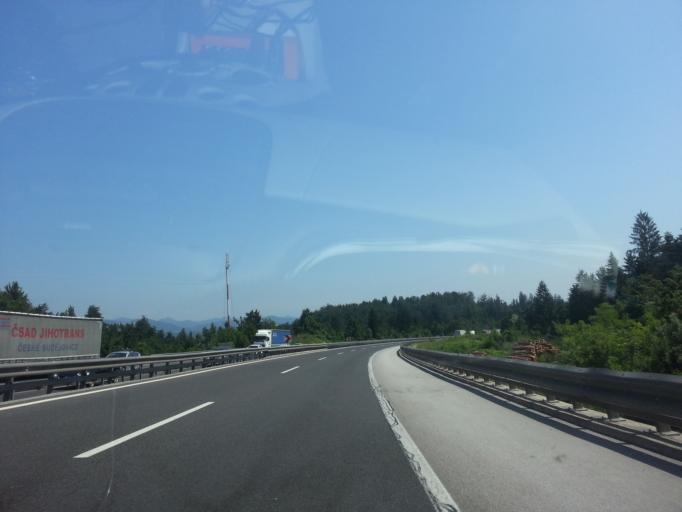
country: SI
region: Vrhnika
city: Vrhnika
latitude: 45.9415
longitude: 14.2778
